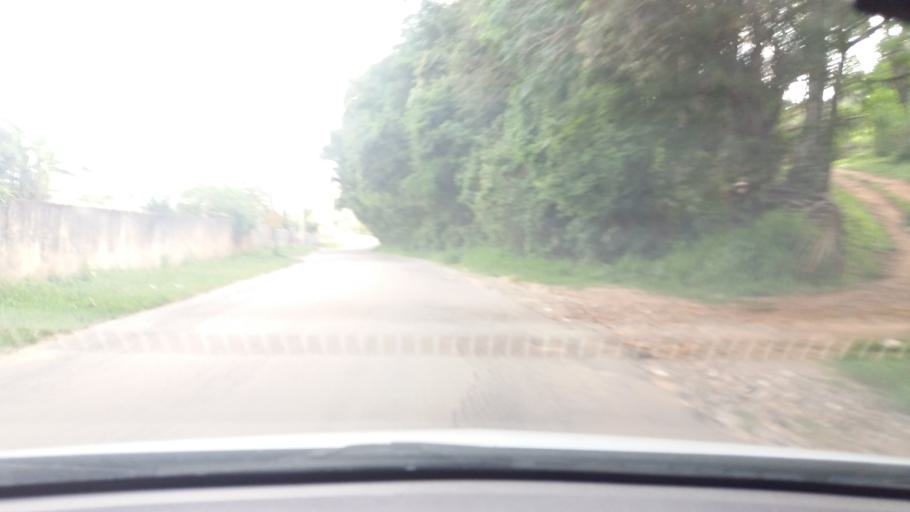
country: BR
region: Sao Paulo
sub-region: Bom Jesus Dos Perdoes
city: Bom Jesus dos Perdoes
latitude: -23.1506
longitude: -46.4706
